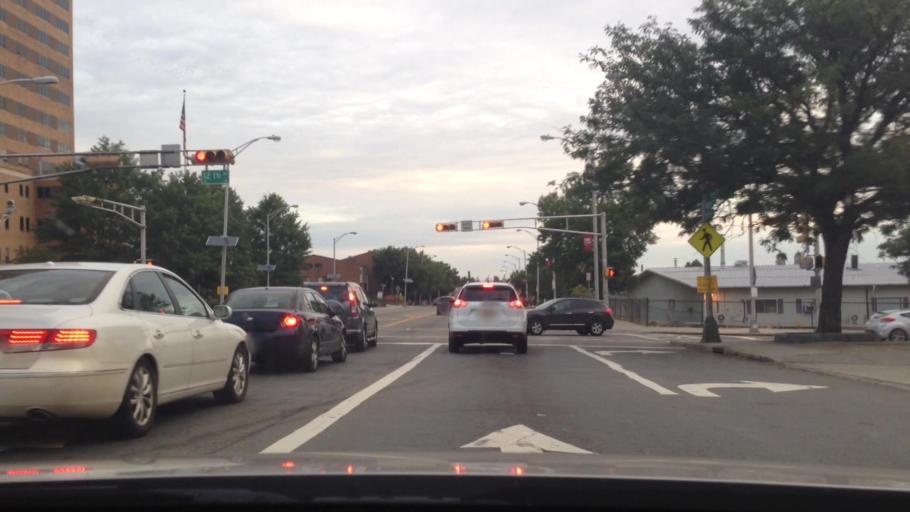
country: US
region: New Jersey
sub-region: Essex County
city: Newark
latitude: 40.7422
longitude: -74.1914
